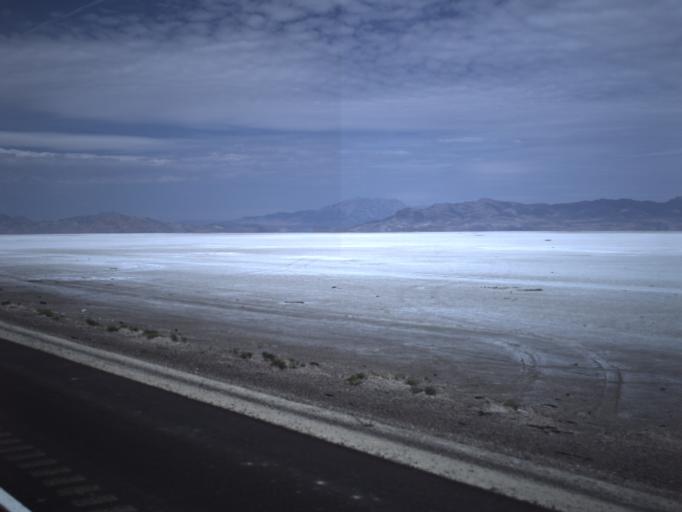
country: US
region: Utah
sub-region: Tooele County
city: Wendover
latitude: 40.7345
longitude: -113.6195
